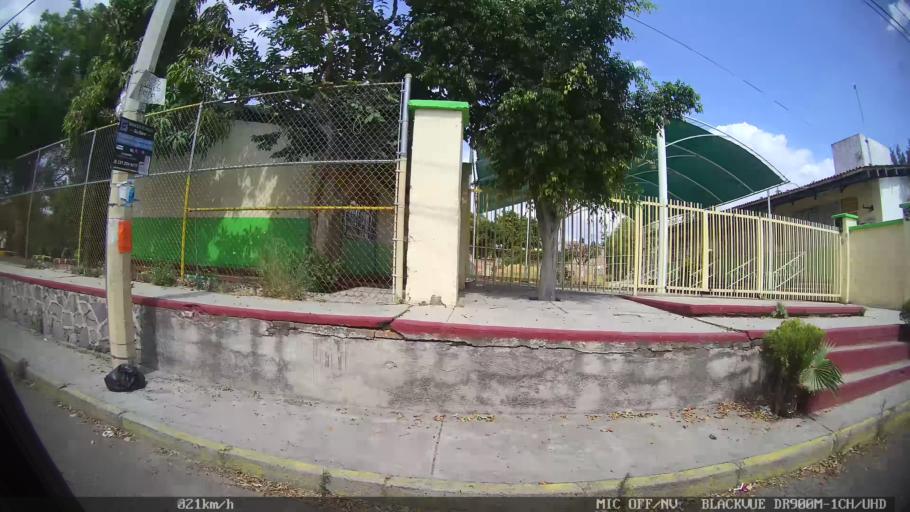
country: MX
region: Jalisco
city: Tlaquepaque
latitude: 20.6254
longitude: -103.2660
